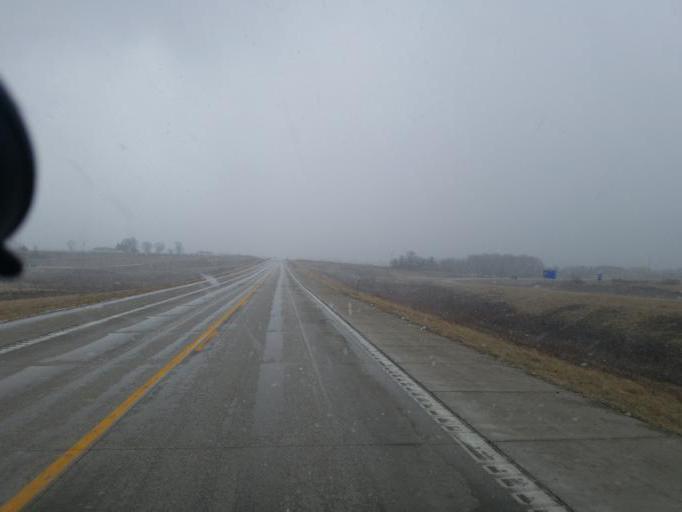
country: US
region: Missouri
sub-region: Adair County
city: Kirksville
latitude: 40.2401
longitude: -92.5800
